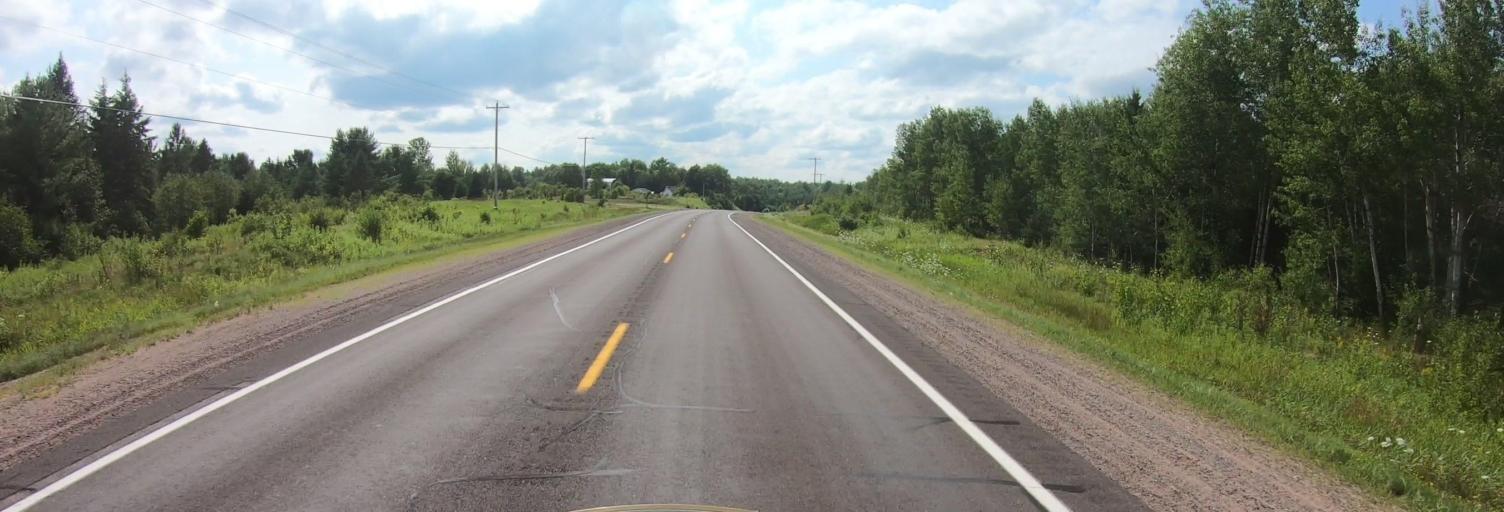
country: US
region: Michigan
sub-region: Ontonagon County
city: Ontonagon
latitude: 46.5335
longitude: -89.1973
